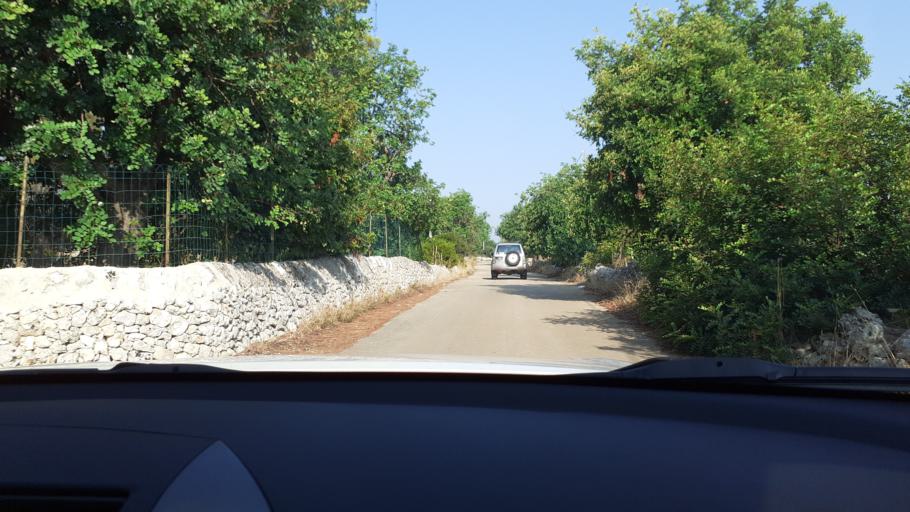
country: IT
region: Sicily
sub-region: Provincia di Siracusa
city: Cassibile
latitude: 36.9782
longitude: 15.1509
